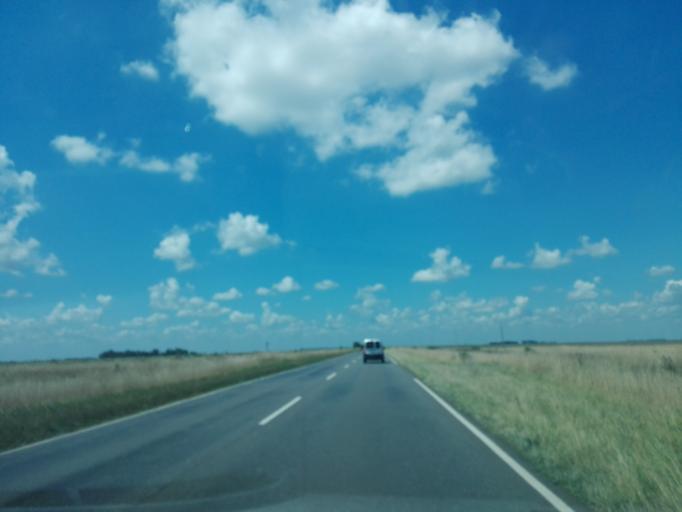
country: AR
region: Buenos Aires
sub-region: Partido de General Belgrano
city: General Belgrano
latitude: -35.9191
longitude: -58.6196
